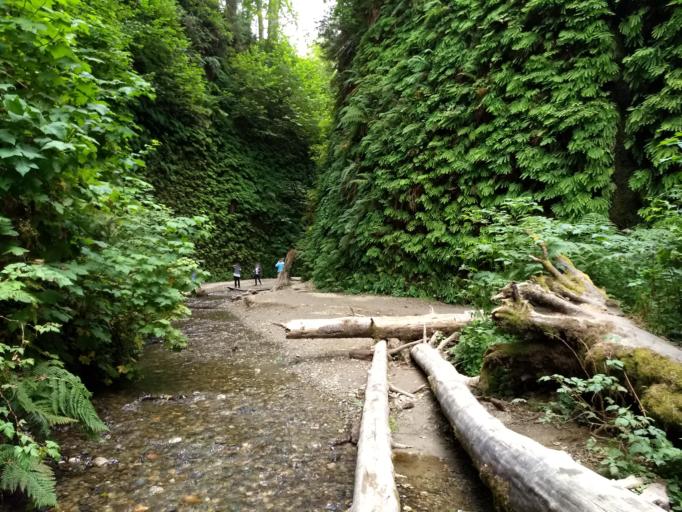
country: US
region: California
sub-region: Humboldt County
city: Westhaven-Moonstone
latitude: 41.4024
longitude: -124.0617
